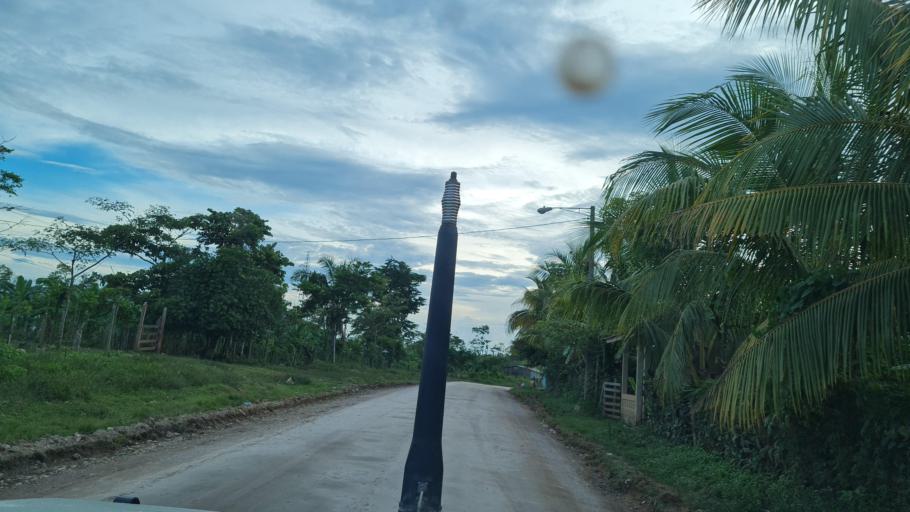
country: NI
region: Atlantico Norte (RAAN)
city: Siuna
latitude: 13.6863
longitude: -84.6143
